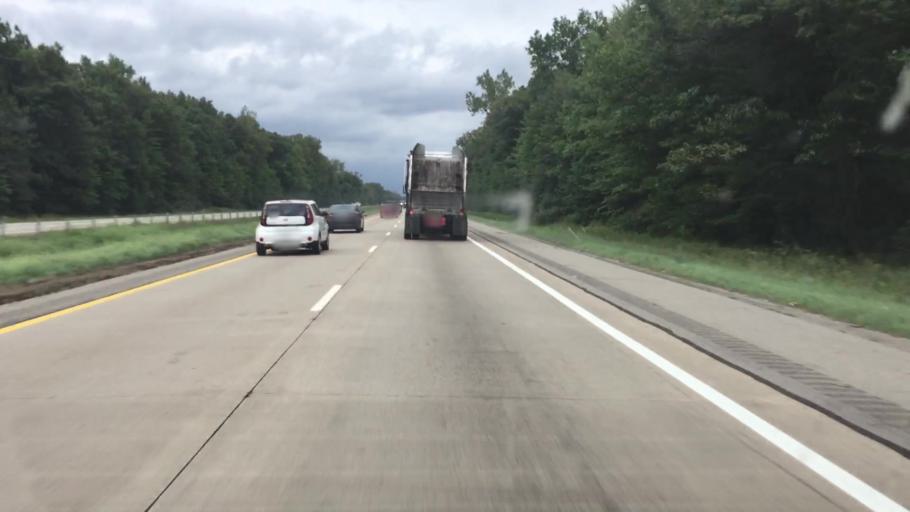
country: US
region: Michigan
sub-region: Monroe County
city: Petersburg
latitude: 41.8851
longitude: -83.6615
